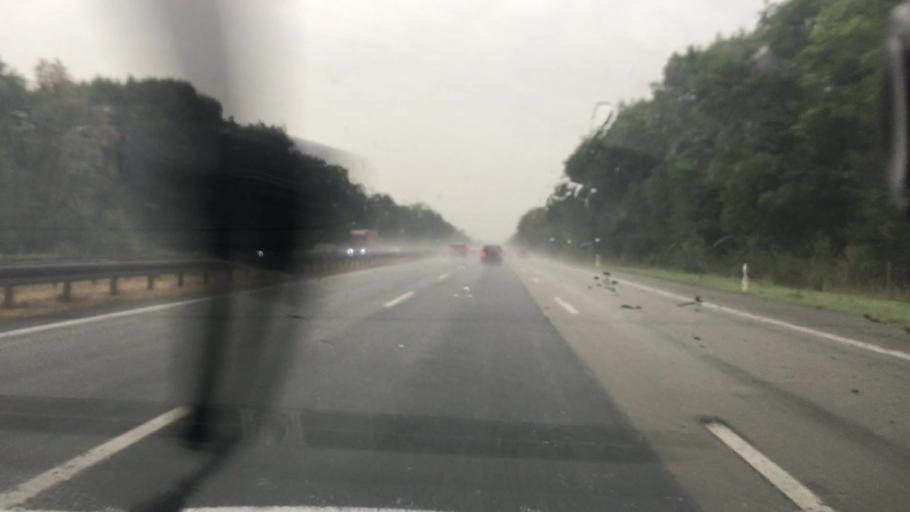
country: DE
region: Hesse
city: Lorsch
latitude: 49.6258
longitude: 8.5553
